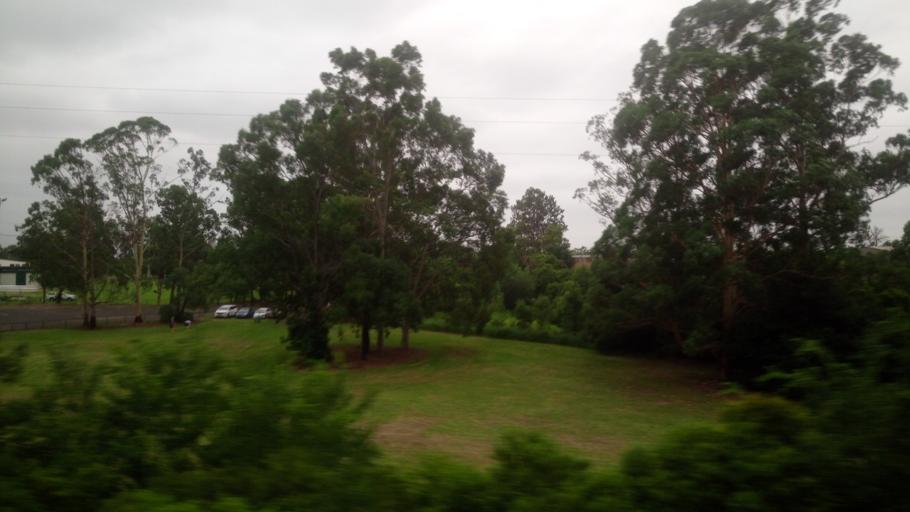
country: AU
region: New South Wales
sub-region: Penrith Municipality
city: Penrith
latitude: -33.7474
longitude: 150.6847
